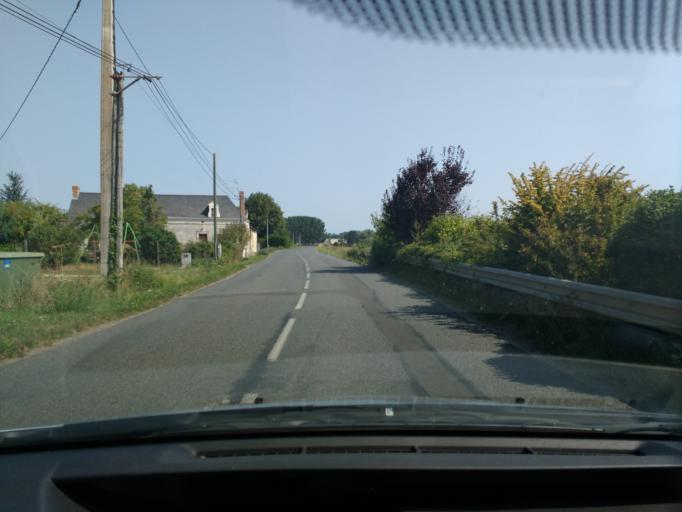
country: FR
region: Pays de la Loire
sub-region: Departement de Maine-et-Loire
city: Baune
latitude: 47.4762
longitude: -0.3176
